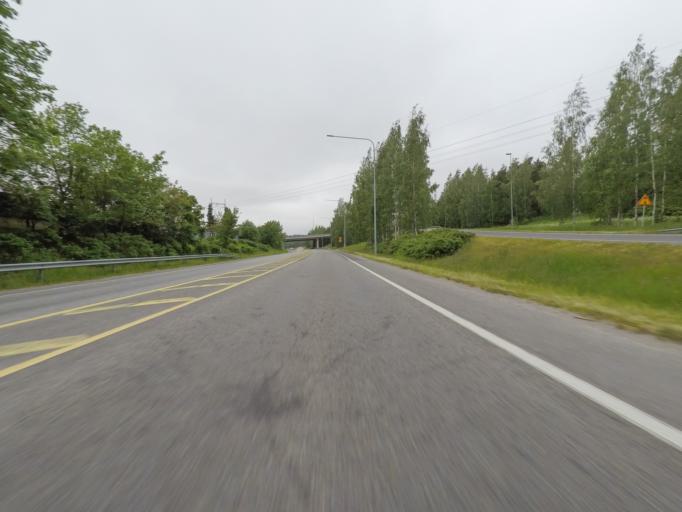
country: FI
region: Varsinais-Suomi
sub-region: Turku
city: Raisio
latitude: 60.4611
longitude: 22.2024
